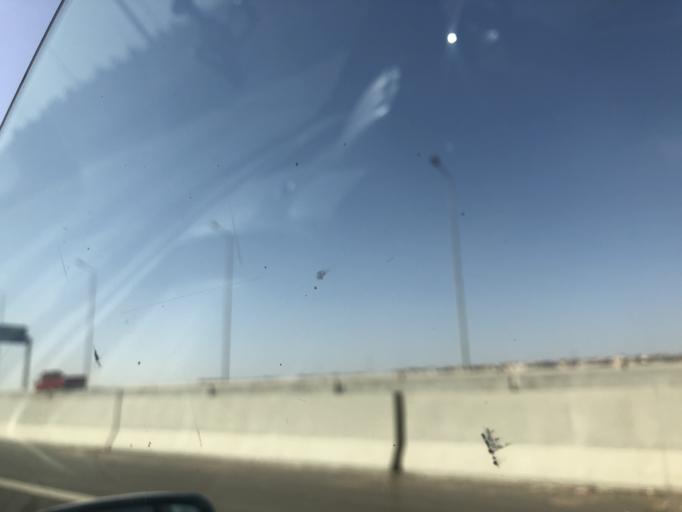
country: EG
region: Al Jizah
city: Madinat Sittah Uktubar
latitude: 29.9685
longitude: 30.8812
